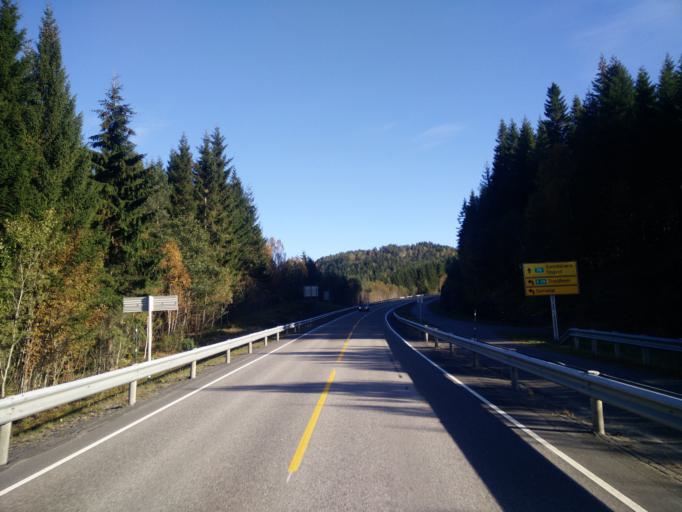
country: NO
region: More og Romsdal
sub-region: Kristiansund
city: Rensvik
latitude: 63.0122
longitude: 7.9924
